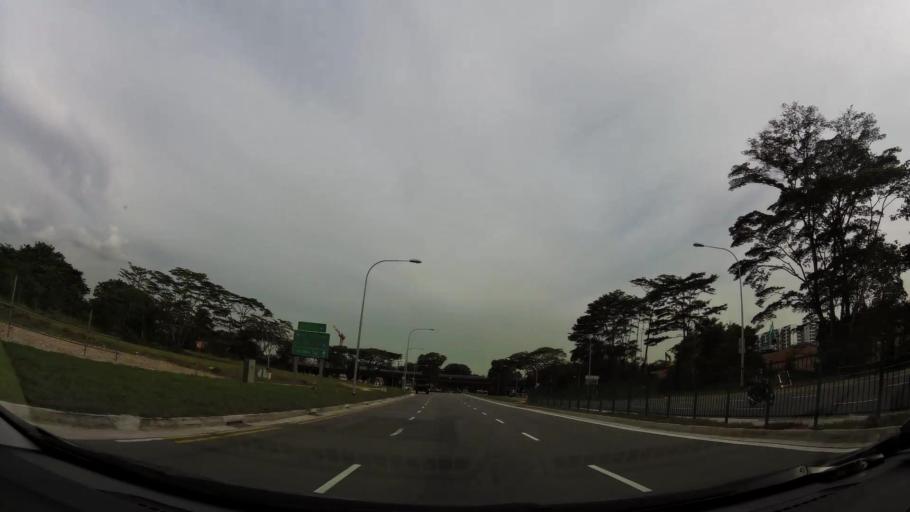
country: MY
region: Johor
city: Johor Bahru
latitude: 1.3561
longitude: 103.6963
